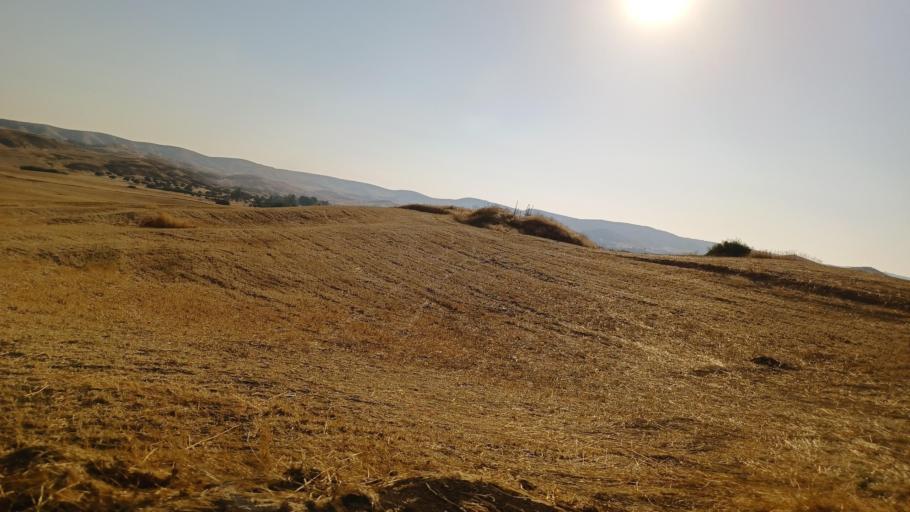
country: CY
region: Larnaka
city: Troulloi
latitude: 35.0089
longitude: 33.6087
